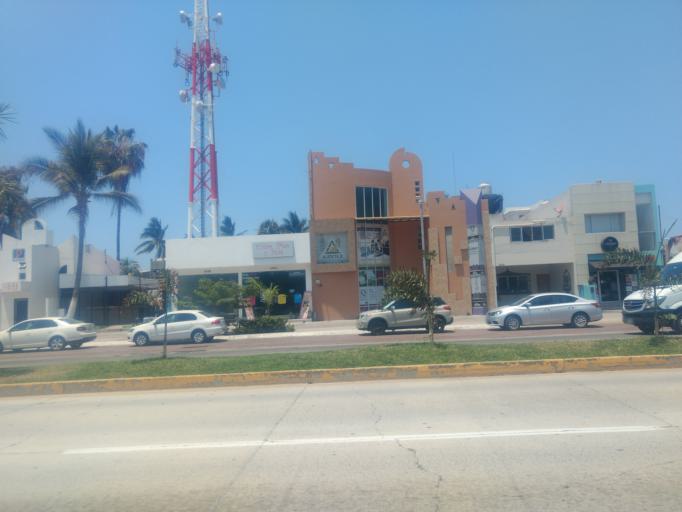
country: MX
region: Colima
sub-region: Manzanillo
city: Manzanillo
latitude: 19.0979
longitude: -104.3222
